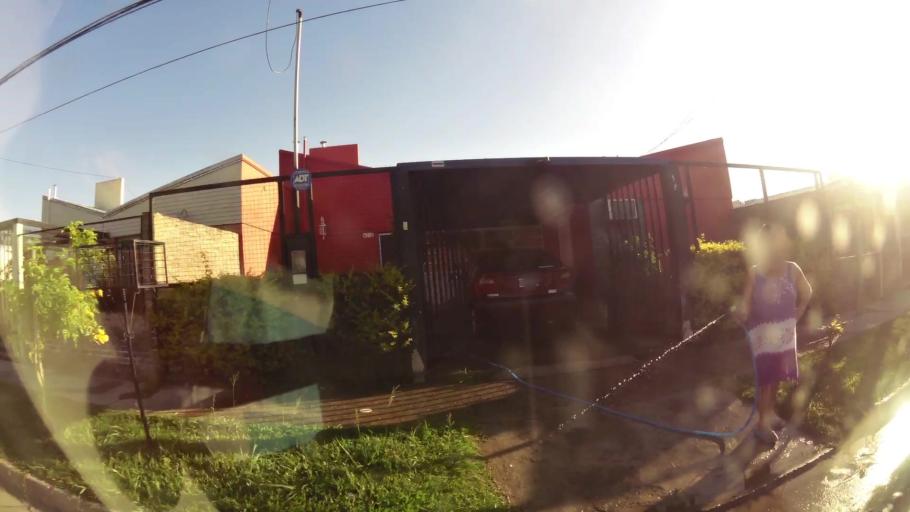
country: AR
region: Santa Fe
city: Santa Fe de la Vera Cruz
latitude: -31.5888
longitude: -60.6893
